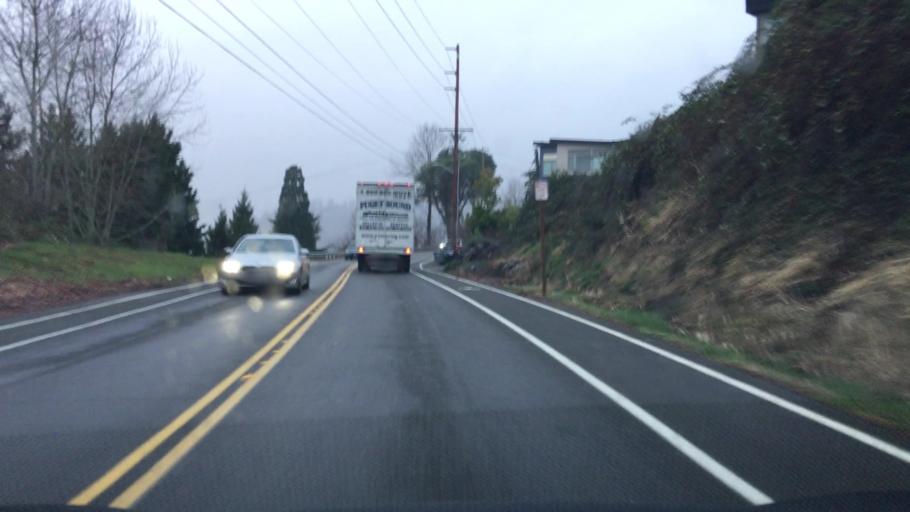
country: US
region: Washington
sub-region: King County
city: Renton
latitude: 47.5167
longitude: -122.2078
